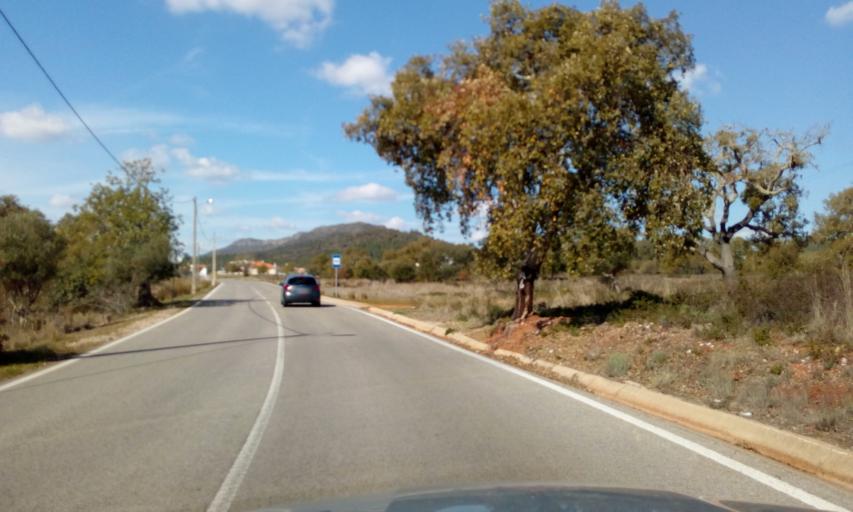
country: PT
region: Faro
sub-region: Loule
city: Loule
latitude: 37.2441
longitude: -8.0613
